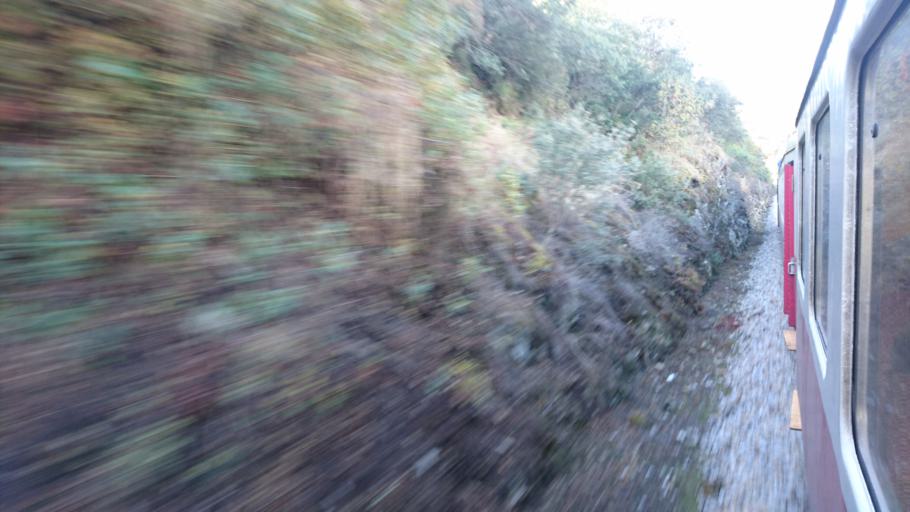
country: PT
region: Guarda
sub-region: Vila Nova de Foz Coa
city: Vila Nova de Foz Coa
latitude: 41.1345
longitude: -7.2133
